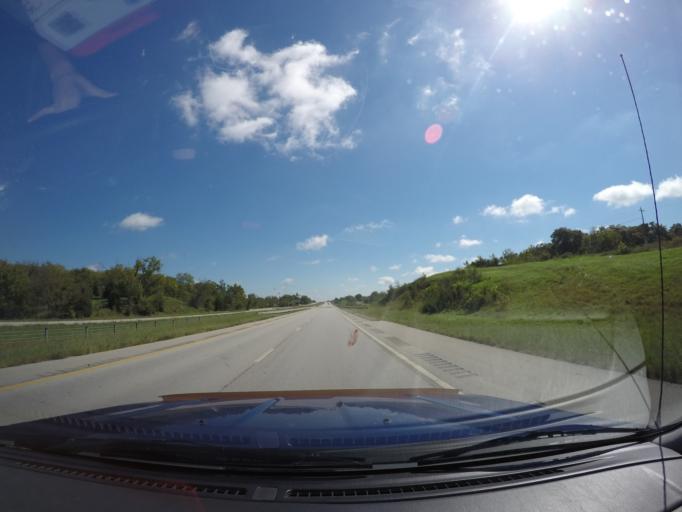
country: US
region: Kansas
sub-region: Douglas County
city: Eudora
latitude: 38.9434
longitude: -95.0628
